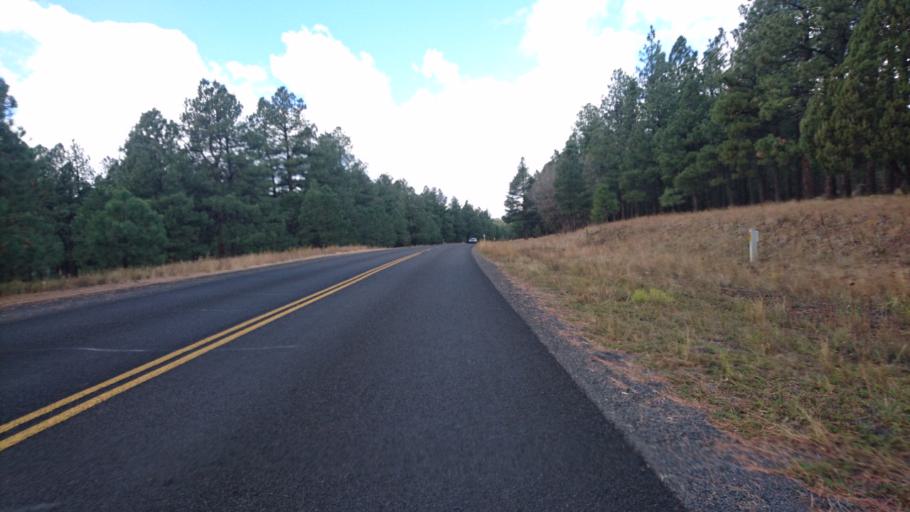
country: US
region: Arizona
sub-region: Coconino County
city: Parks
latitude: 35.2583
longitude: -111.9407
